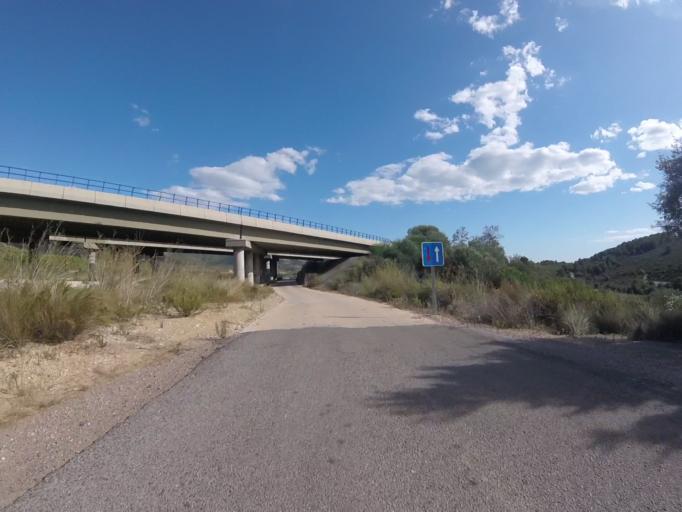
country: ES
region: Valencia
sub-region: Provincia de Castello
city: Alcala de Xivert
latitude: 40.2746
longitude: 0.2337
